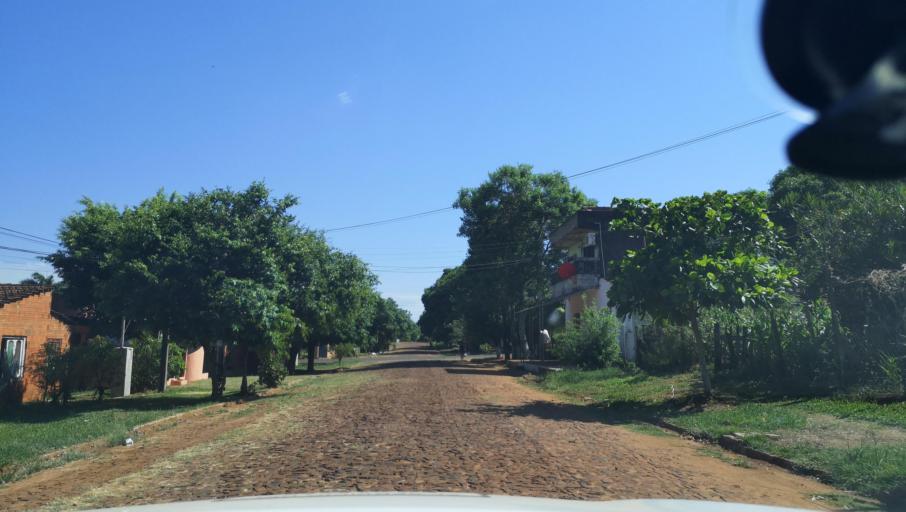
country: PY
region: Itapua
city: Carmen del Parana
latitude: -27.1656
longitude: -56.2313
